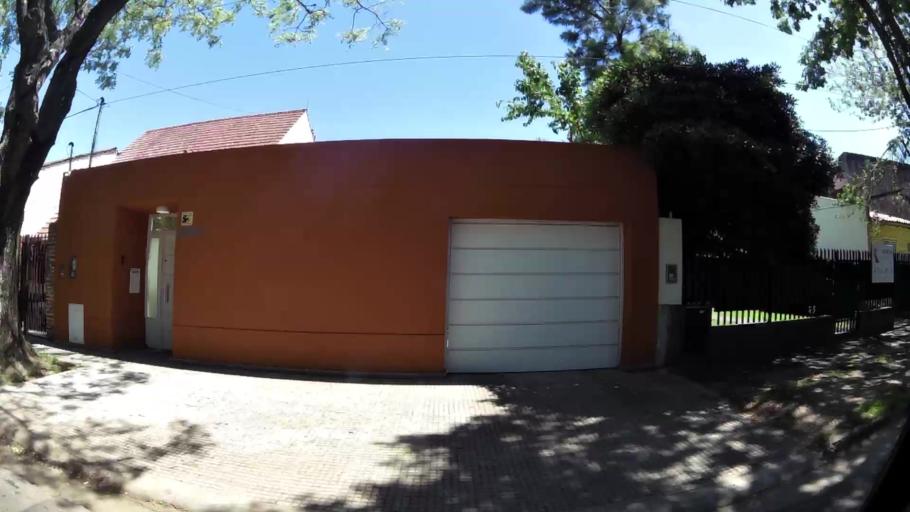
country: AR
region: Buenos Aires
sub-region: Partido de Vicente Lopez
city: Olivos
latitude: -34.5072
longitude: -58.5093
